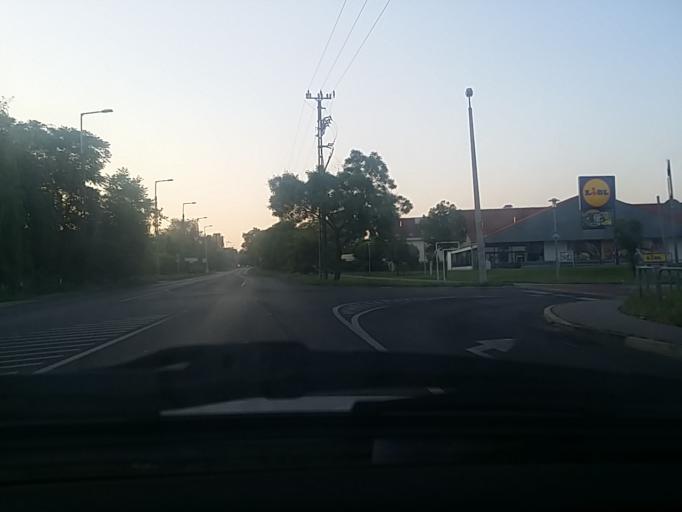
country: HU
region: Budapest
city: Budapest XVII. keruelet
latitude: 47.4735
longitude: 19.2740
